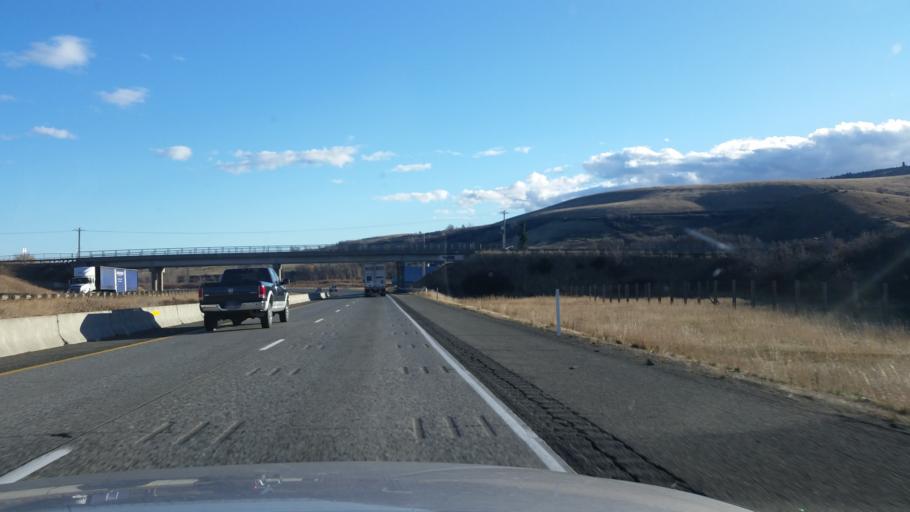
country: US
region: Washington
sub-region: Kittitas County
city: Ellensburg
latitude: 47.0870
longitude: -120.7423
